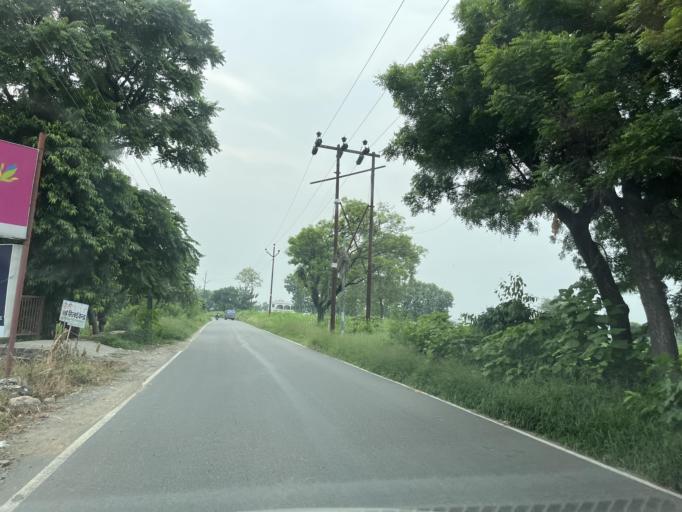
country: IN
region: Uttarakhand
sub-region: Naini Tal
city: Haldwani
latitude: 29.1736
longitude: 79.4784
